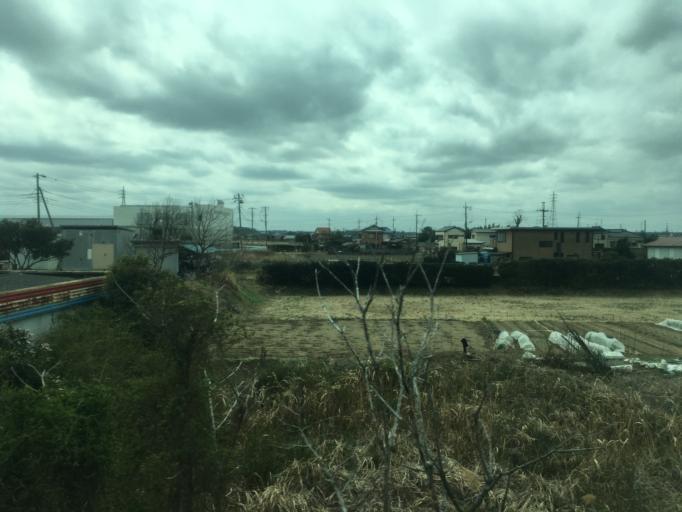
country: JP
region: Ibaraki
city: Ryugasaki
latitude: 35.8439
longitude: 140.1366
